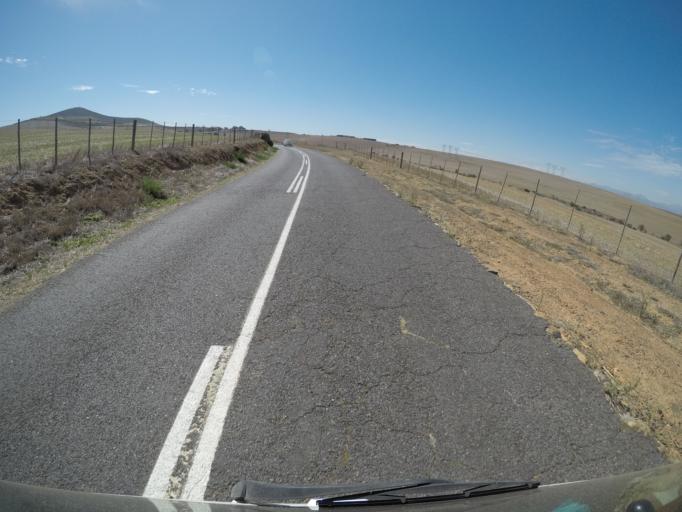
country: ZA
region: Western Cape
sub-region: City of Cape Town
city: Sunset Beach
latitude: -33.7384
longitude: 18.5656
